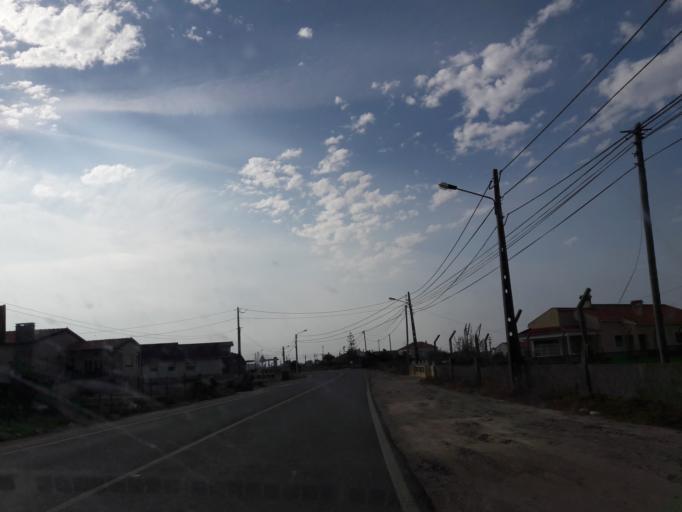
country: PT
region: Leiria
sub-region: Peniche
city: Atouguia da Baleia
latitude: 39.3436
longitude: -9.3371
